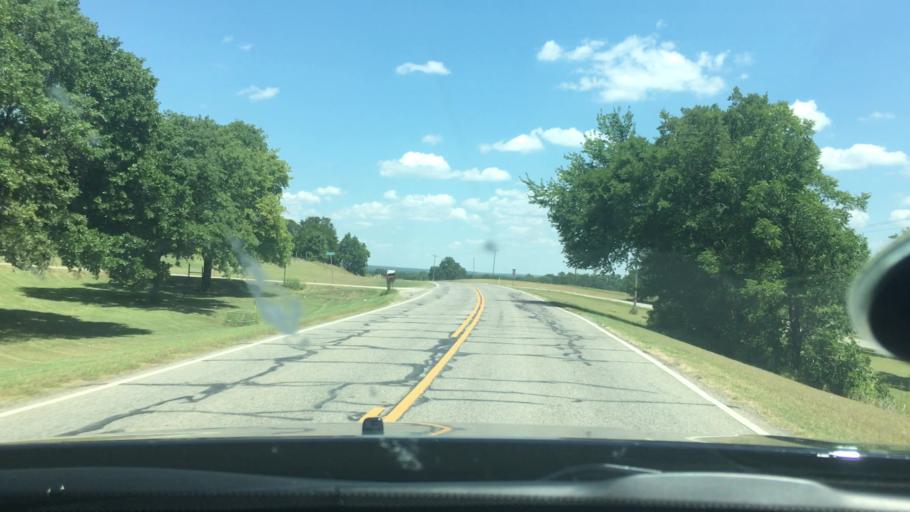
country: US
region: Oklahoma
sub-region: Carter County
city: Dickson
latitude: 34.2028
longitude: -96.9782
